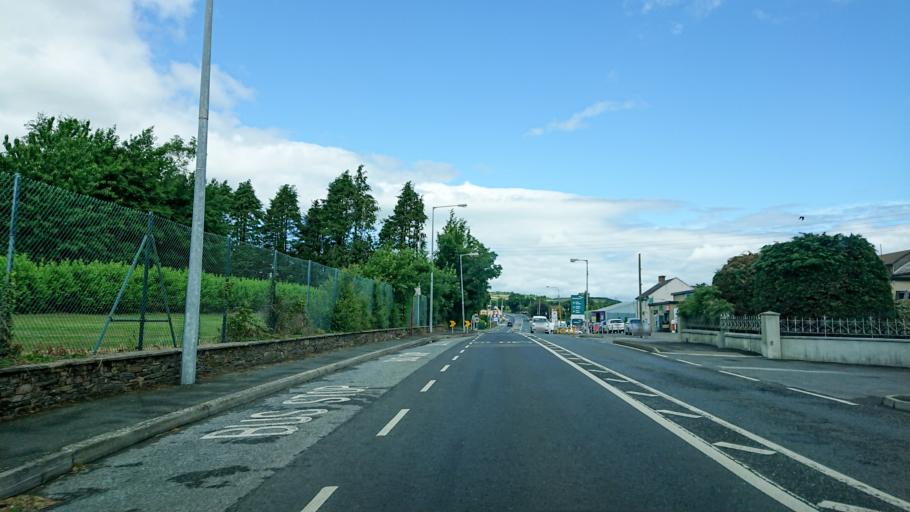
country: IE
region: Leinster
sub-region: Kilkenny
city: Mooncoin
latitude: 52.2323
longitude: -7.2416
